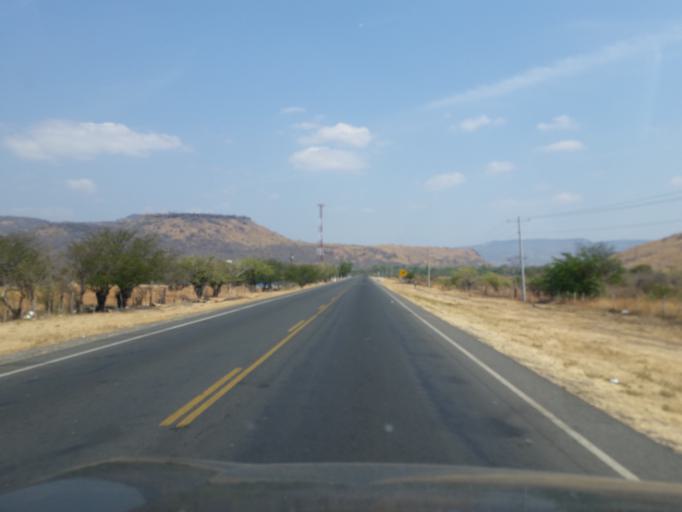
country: NI
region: Managua
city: Tipitapa
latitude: 12.4302
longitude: -86.0420
